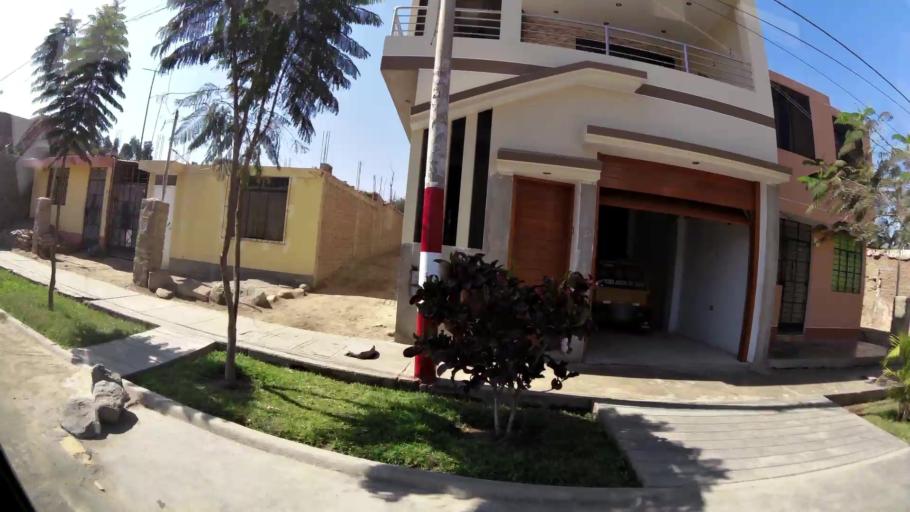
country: PE
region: Ica
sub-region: Provincia de Ica
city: Guadalupe
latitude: -13.9315
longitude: -75.6703
